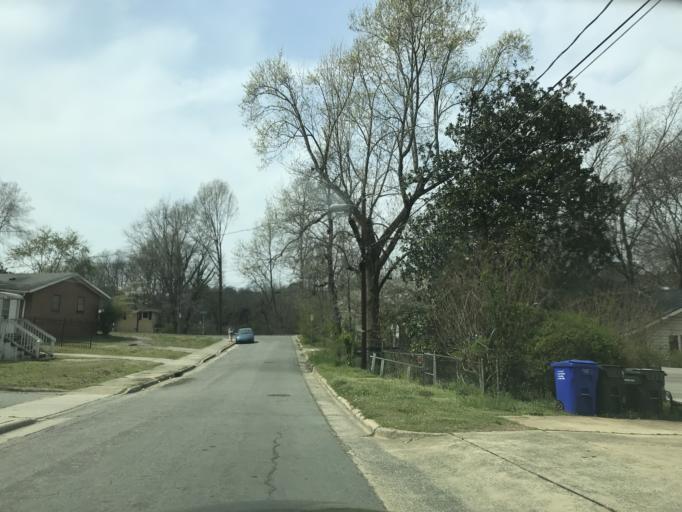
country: US
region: North Carolina
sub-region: Orange County
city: Carrboro
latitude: 35.9155
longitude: -79.0665
